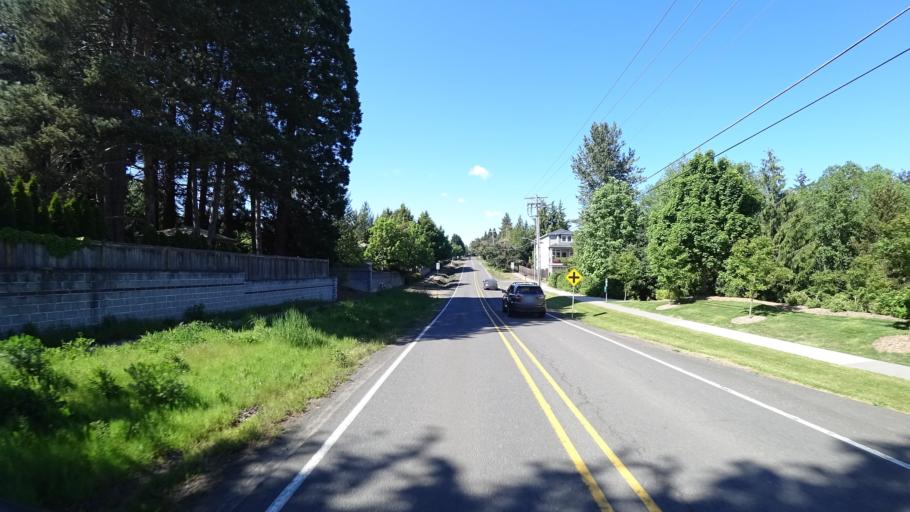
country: US
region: Oregon
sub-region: Washington County
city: Oak Hills
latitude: 45.5495
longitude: -122.8302
